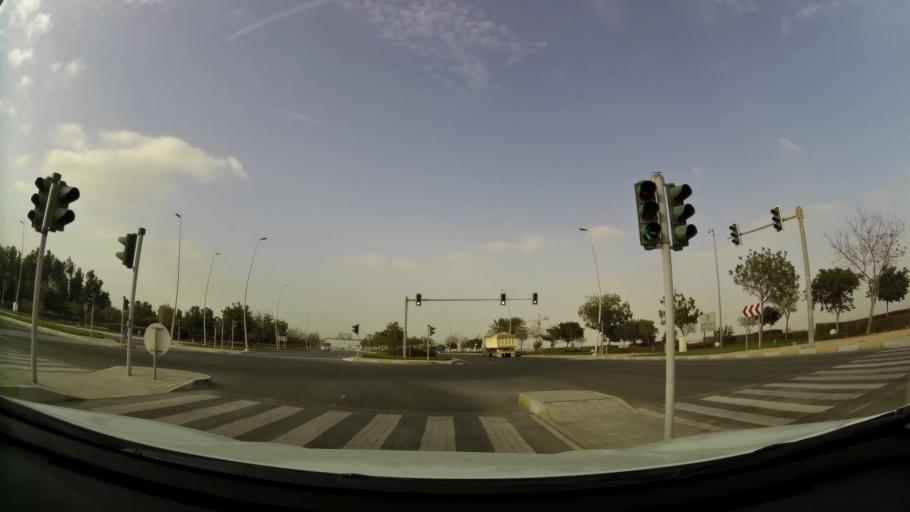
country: AE
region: Abu Dhabi
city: Abu Dhabi
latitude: 24.4908
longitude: 54.6315
